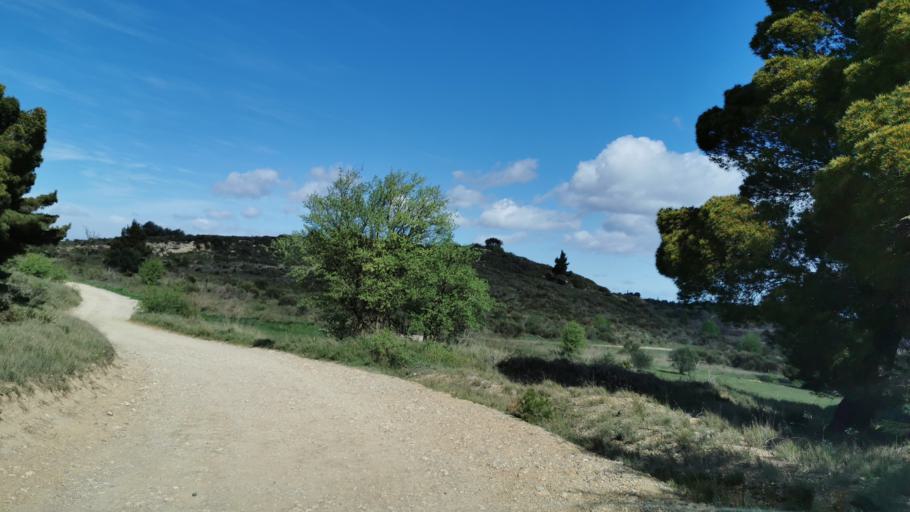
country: FR
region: Languedoc-Roussillon
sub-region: Departement de l'Aude
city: Narbonne
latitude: 43.1462
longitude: 2.9843
